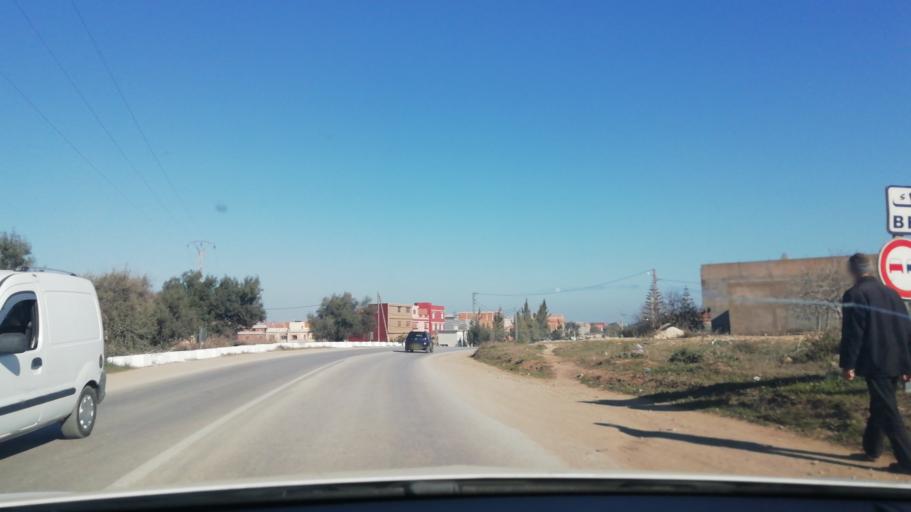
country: DZ
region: Tlemcen
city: Nedroma
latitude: 35.0120
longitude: -1.8994
